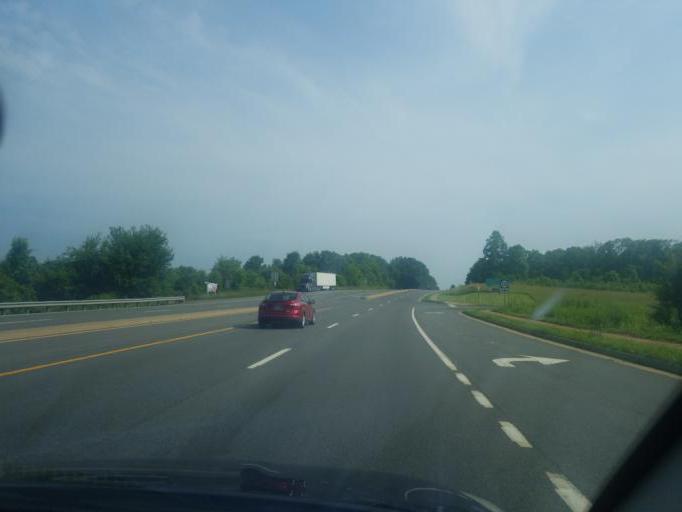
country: US
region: Virginia
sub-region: Culpeper County
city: Culpeper
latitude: 38.4469
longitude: -78.0234
